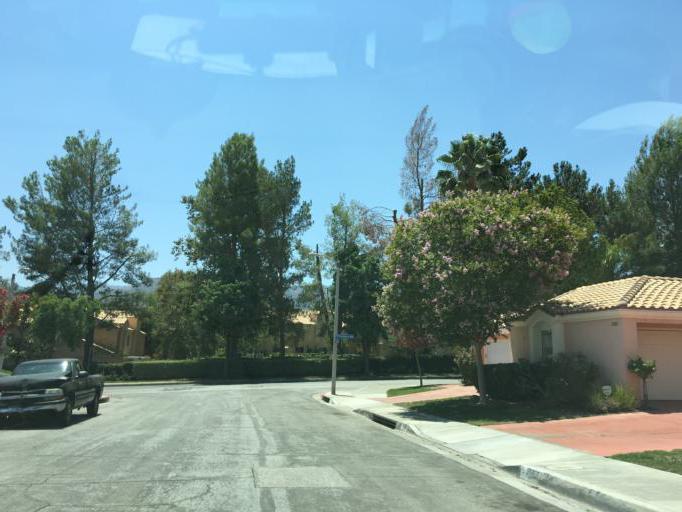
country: US
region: California
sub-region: Los Angeles County
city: Santa Clarita
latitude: 34.3897
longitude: -118.5768
